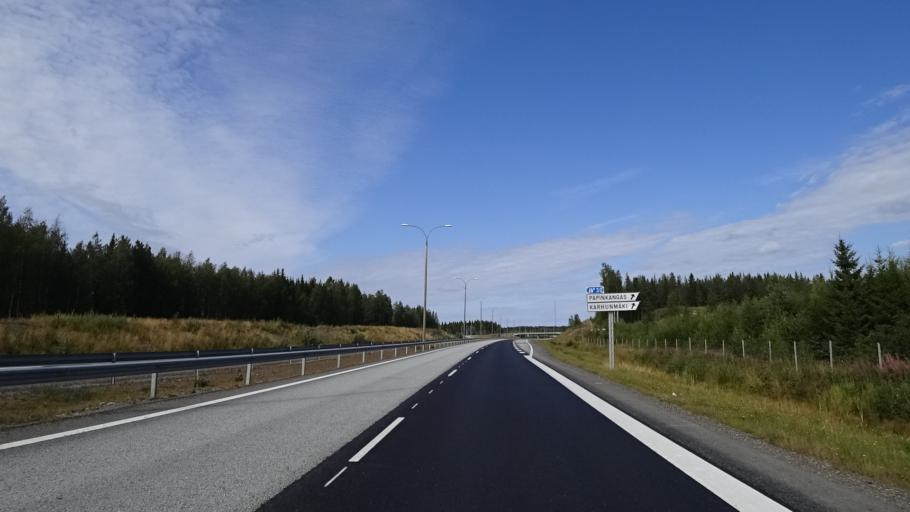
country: FI
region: North Karelia
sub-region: Joensuu
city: Joensuu
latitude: 62.5615
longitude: 29.8358
